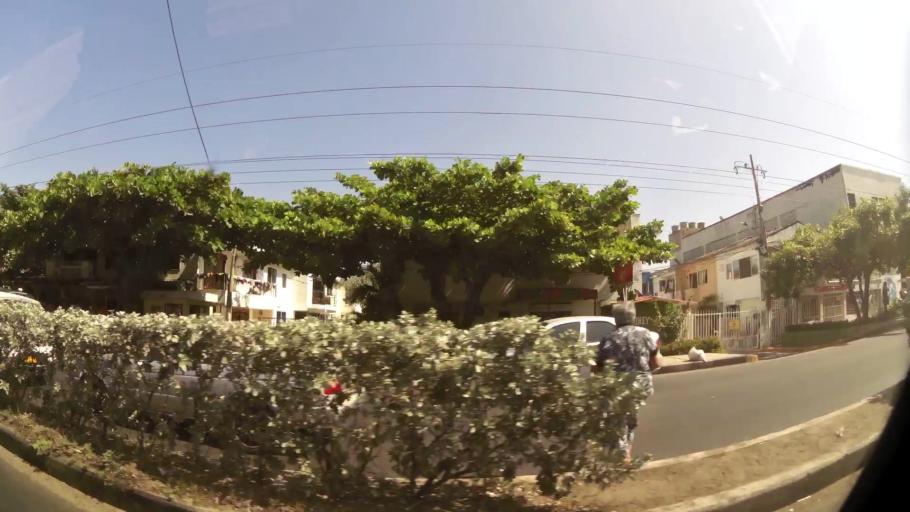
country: CO
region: Bolivar
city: Cartagena
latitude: 10.3849
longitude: -75.4699
